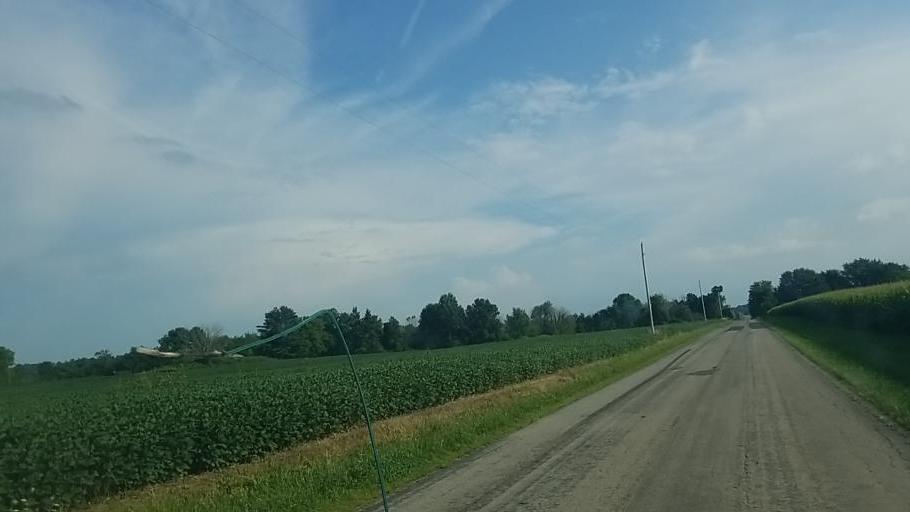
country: US
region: Ohio
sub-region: Wayne County
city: West Salem
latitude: 40.8864
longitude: -82.0734
